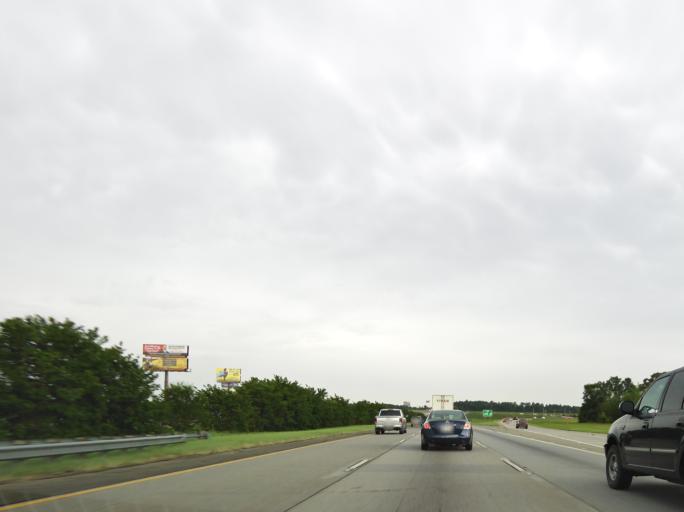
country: US
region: Georgia
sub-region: Peach County
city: Byron
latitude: 32.5933
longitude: -83.7431
